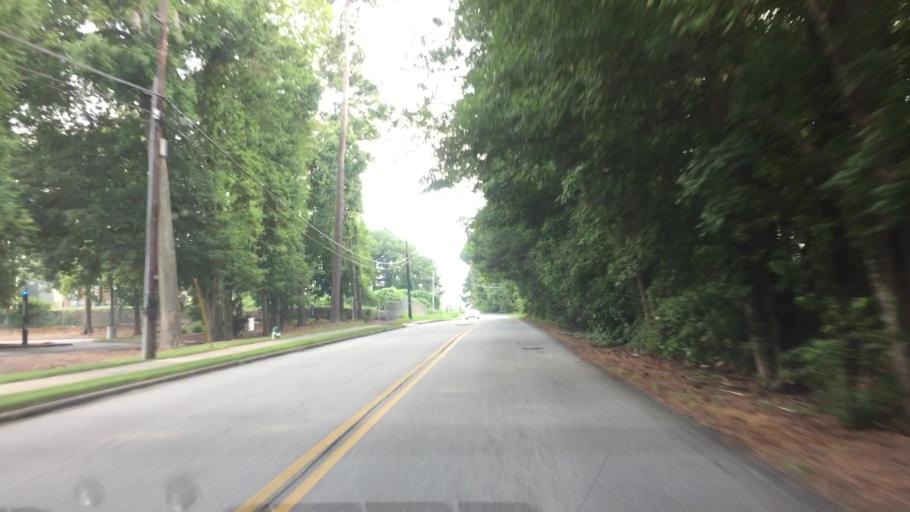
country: US
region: Georgia
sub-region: DeKalb County
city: Avondale Estates
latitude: 33.7818
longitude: -84.2794
